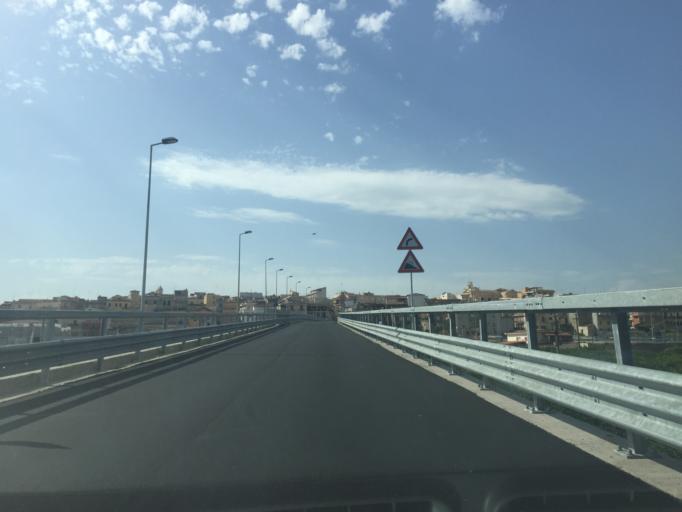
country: IT
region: Sicily
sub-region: Provincia di Siracusa
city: Rosolini
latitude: 36.8165
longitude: 14.9550
